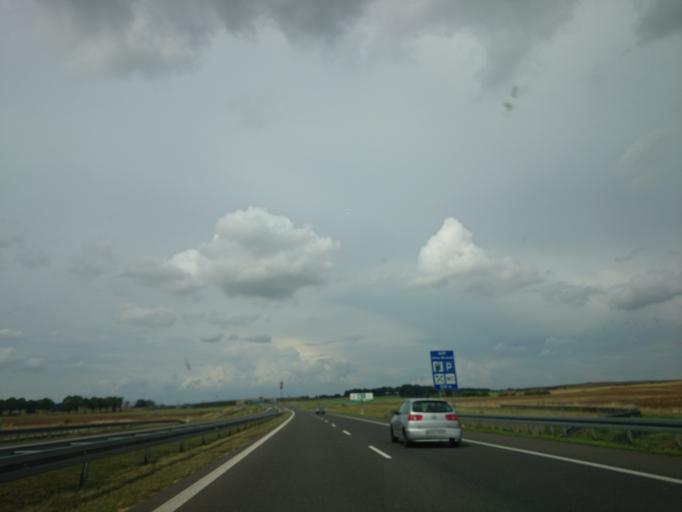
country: PL
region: West Pomeranian Voivodeship
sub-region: Powiat pyrzycki
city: Kozielice
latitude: 53.0409
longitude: 14.8656
